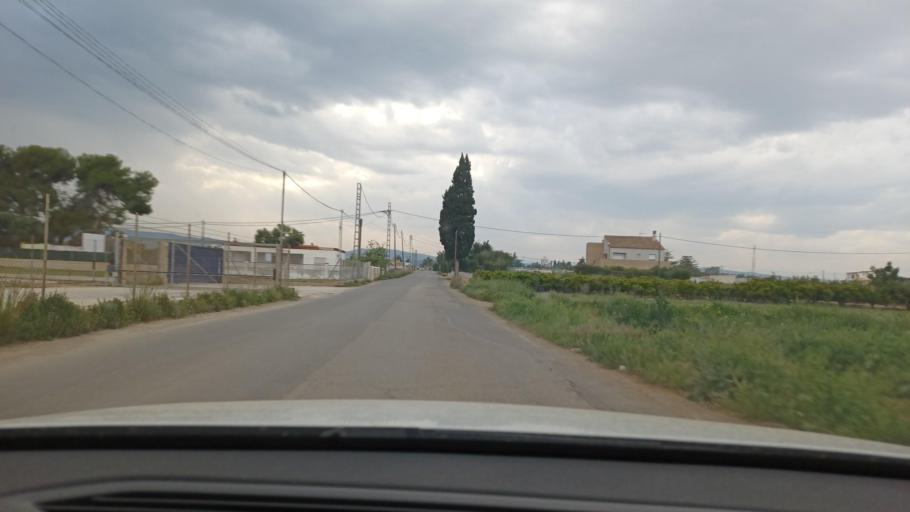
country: ES
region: Valencia
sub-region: Provincia de Castello
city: Benicarlo
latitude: 40.4042
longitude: 0.4065
